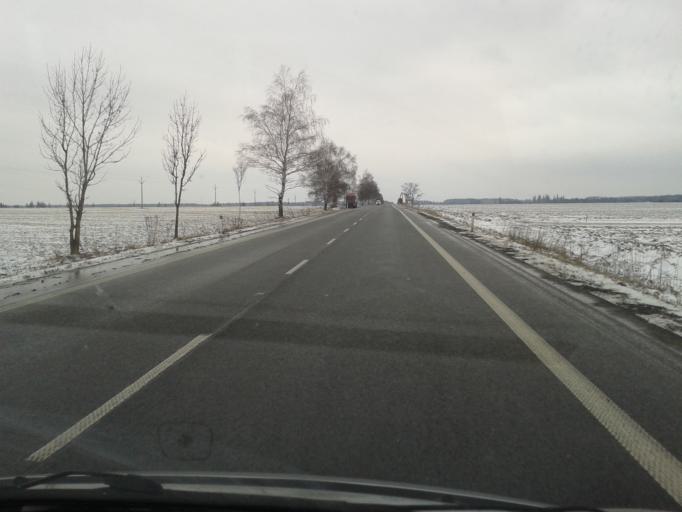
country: SK
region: Zilinsky
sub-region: Okres Zilina
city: Trstena
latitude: 49.3887
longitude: 19.6398
